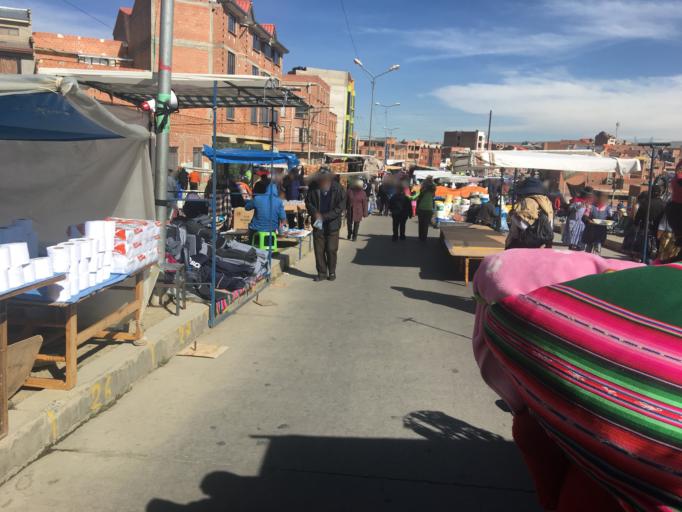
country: BO
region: La Paz
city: La Paz
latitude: -16.4923
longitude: -68.1701
